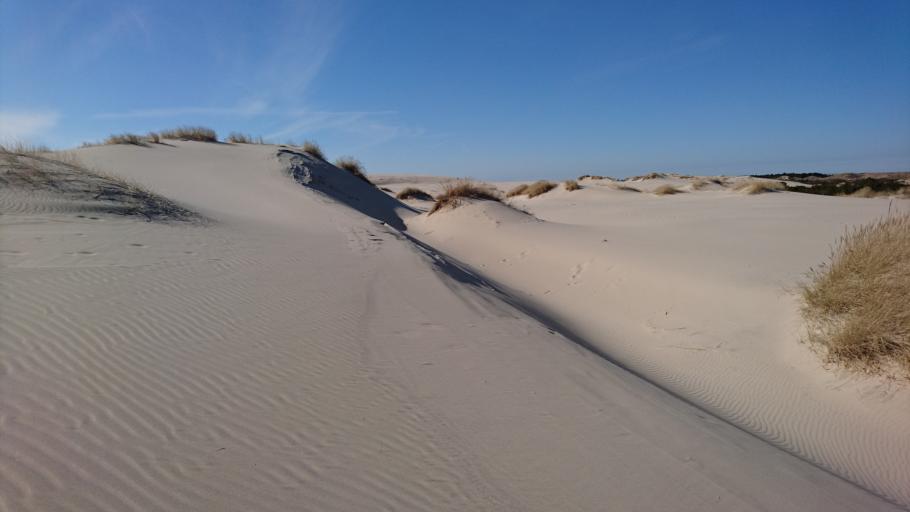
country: DK
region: North Denmark
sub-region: Frederikshavn Kommune
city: Strandby
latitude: 57.6492
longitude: 10.4155
